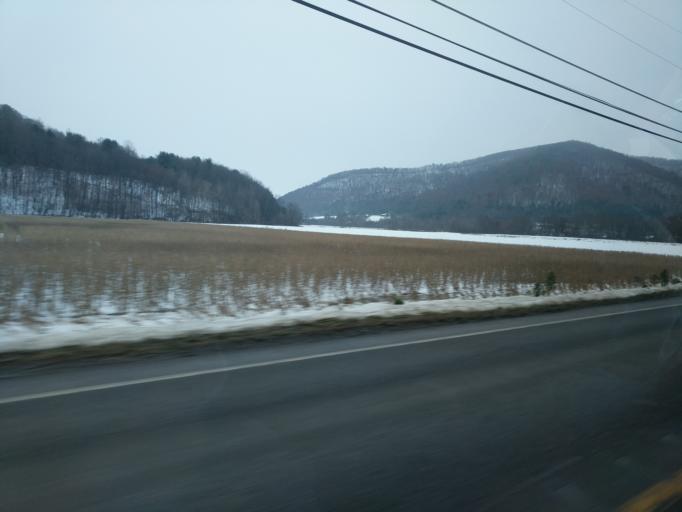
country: US
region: Pennsylvania
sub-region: Tioga County
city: Wellsboro
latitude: 41.8404
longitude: -77.2787
